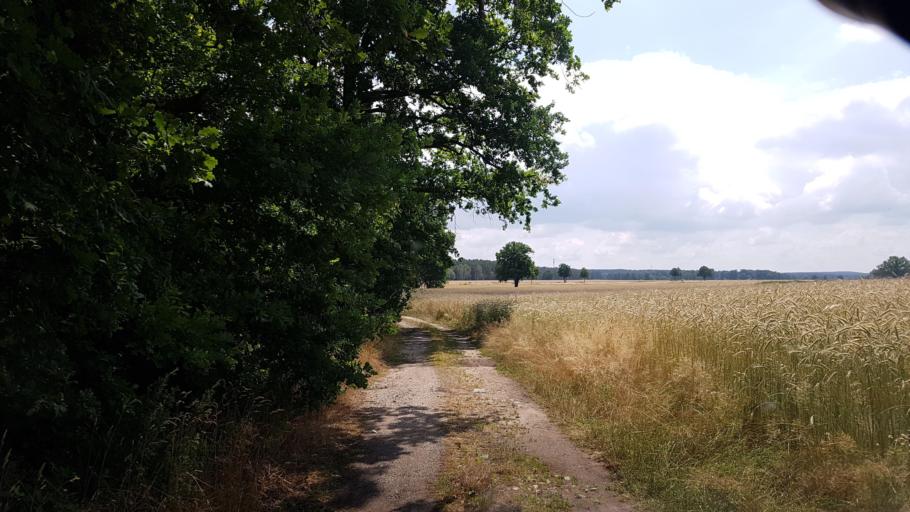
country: DE
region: Brandenburg
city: Crinitz
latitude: 51.7536
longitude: 13.8550
